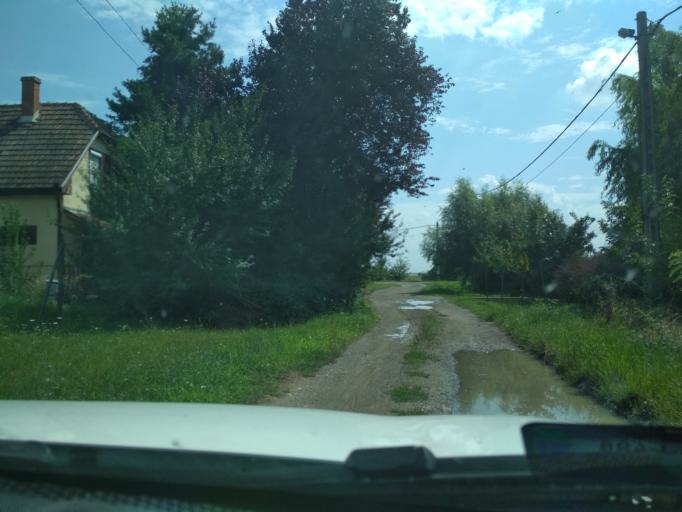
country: HU
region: Jasz-Nagykun-Szolnok
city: Abadszalok
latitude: 47.4693
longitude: 20.5769
